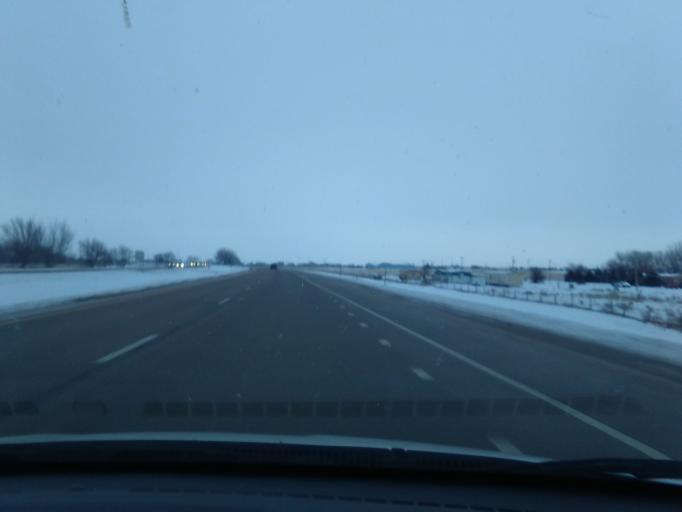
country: US
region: Nebraska
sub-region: Keith County
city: Ogallala
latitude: 41.1150
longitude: -101.7073
